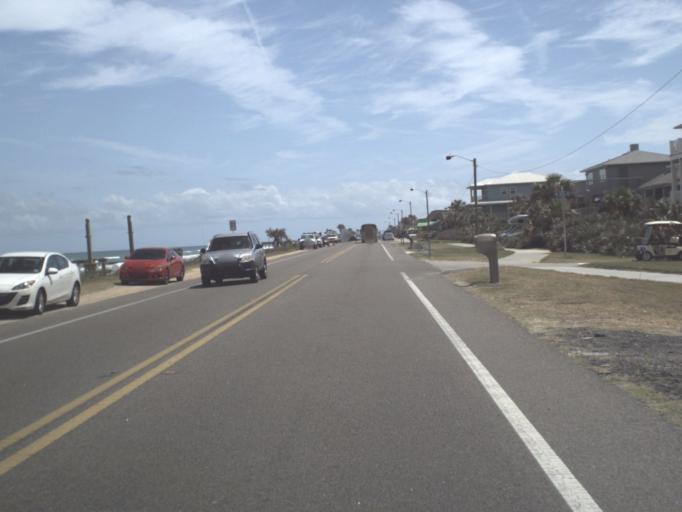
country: US
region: Florida
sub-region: Flagler County
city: Flagler Beach
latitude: 29.4898
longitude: -81.1318
